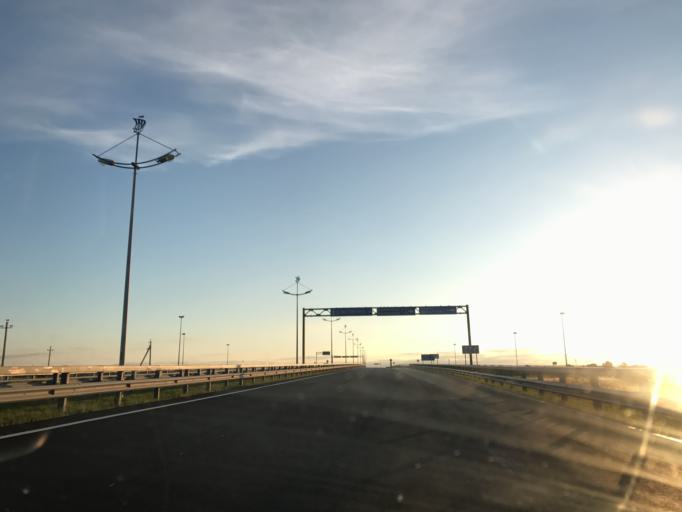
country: RU
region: Kaliningrad
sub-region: Gorod Kaliningrad
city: Pionerskiy
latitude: 54.9213
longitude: 20.3344
